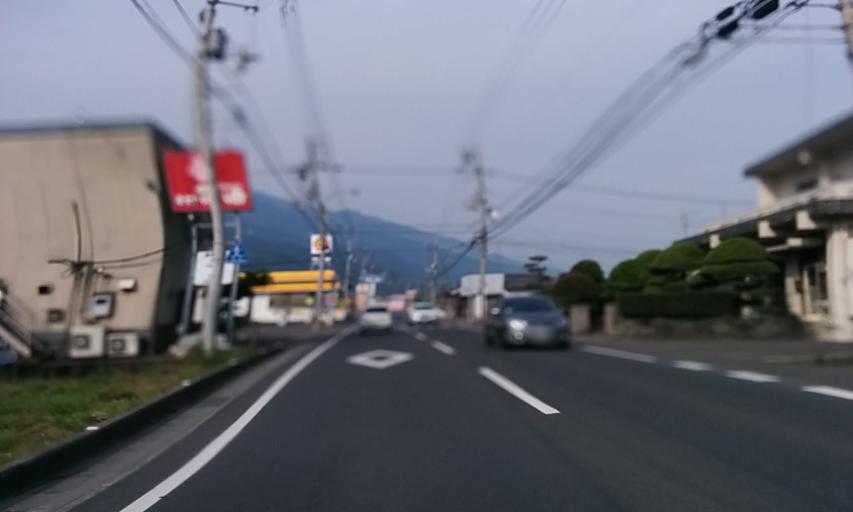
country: JP
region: Ehime
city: Kawanoecho
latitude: 33.9717
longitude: 133.5250
